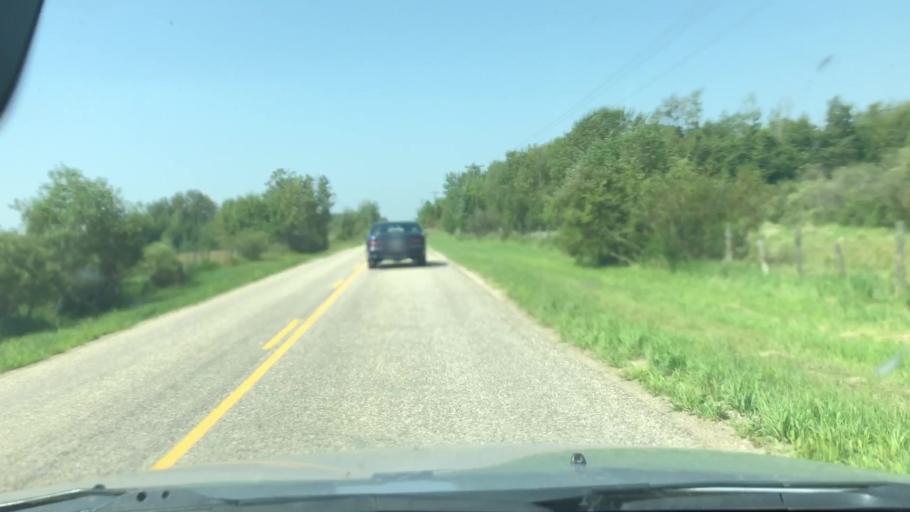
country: CA
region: Alberta
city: Devon
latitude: 53.4253
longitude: -113.8010
